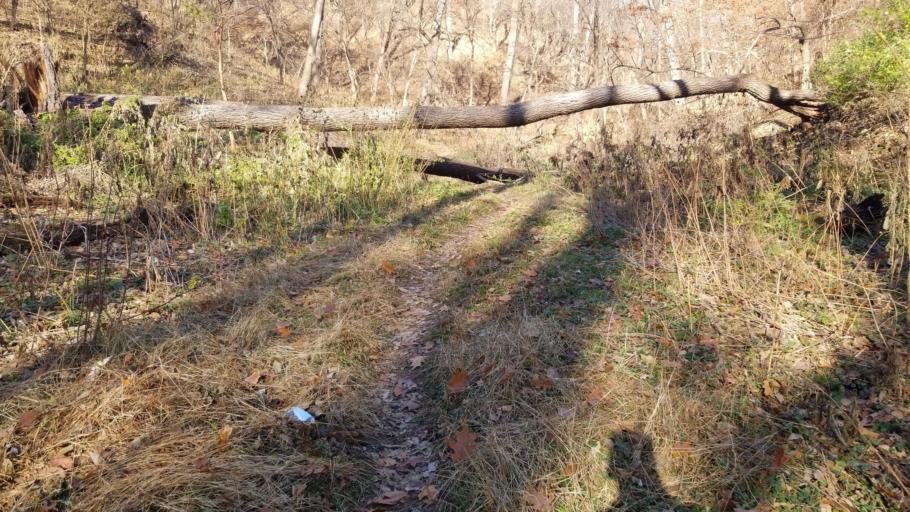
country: US
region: Nebraska
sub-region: Sarpy County
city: Bellevue
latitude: 41.1639
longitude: -95.8948
